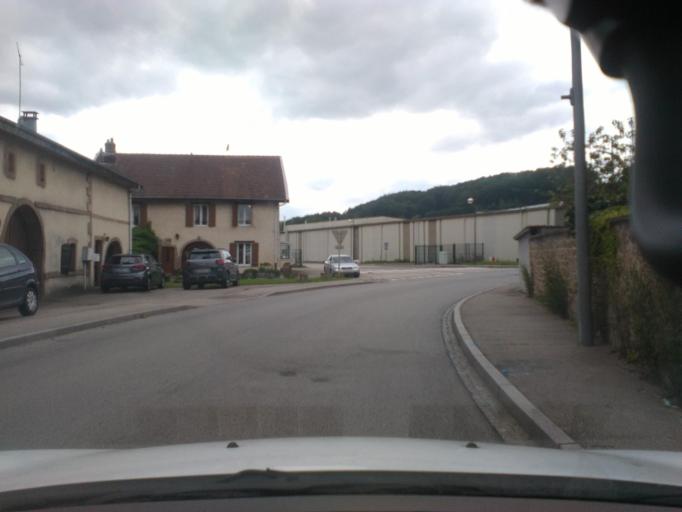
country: FR
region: Lorraine
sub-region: Departement des Vosges
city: Bruyeres
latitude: 48.1721
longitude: 6.6708
